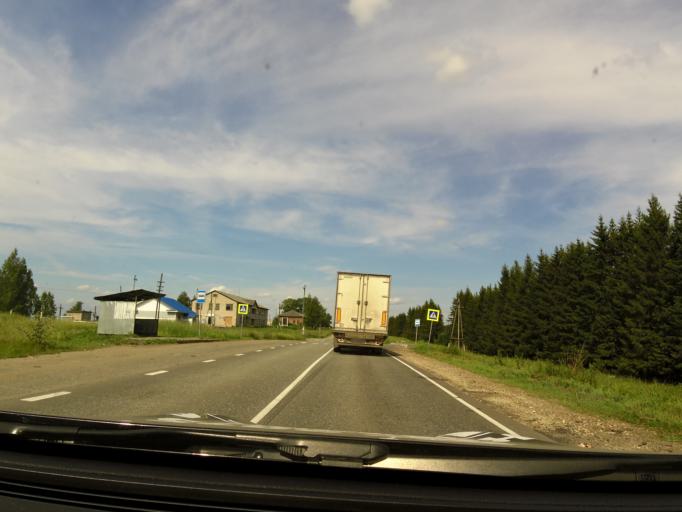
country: RU
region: Kirov
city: Slobodskoy
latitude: 58.7472
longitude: 50.3084
